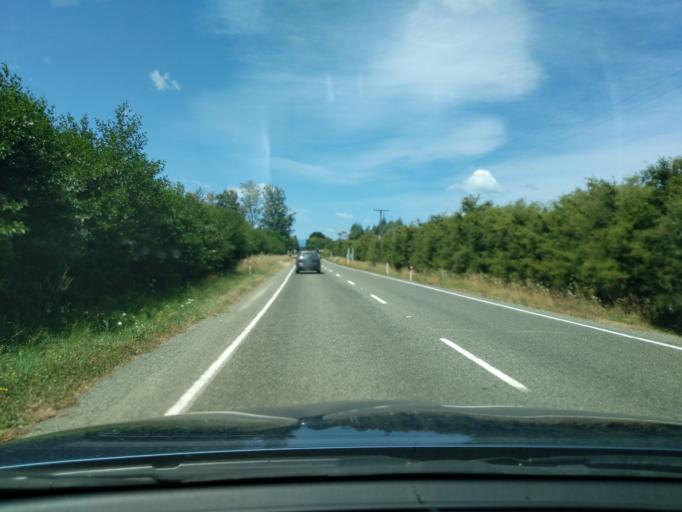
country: NZ
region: Tasman
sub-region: Tasman District
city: Motueka
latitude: -41.0573
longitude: 172.9668
